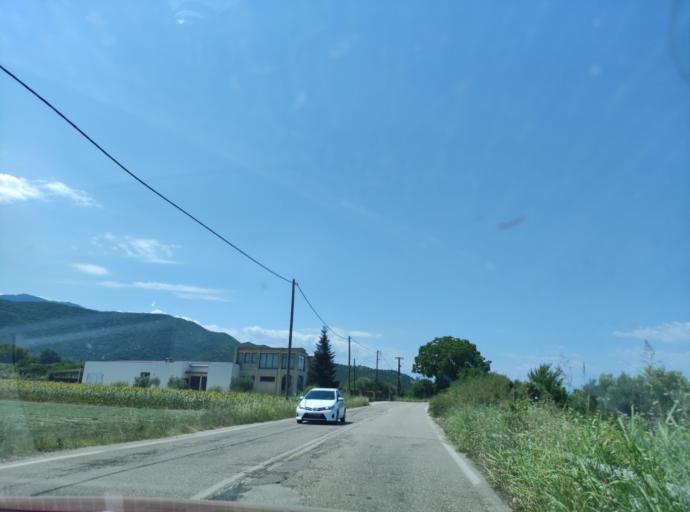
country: GR
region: East Macedonia and Thrace
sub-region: Nomos Kavalas
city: Palaiochori
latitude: 40.9578
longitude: 24.1910
